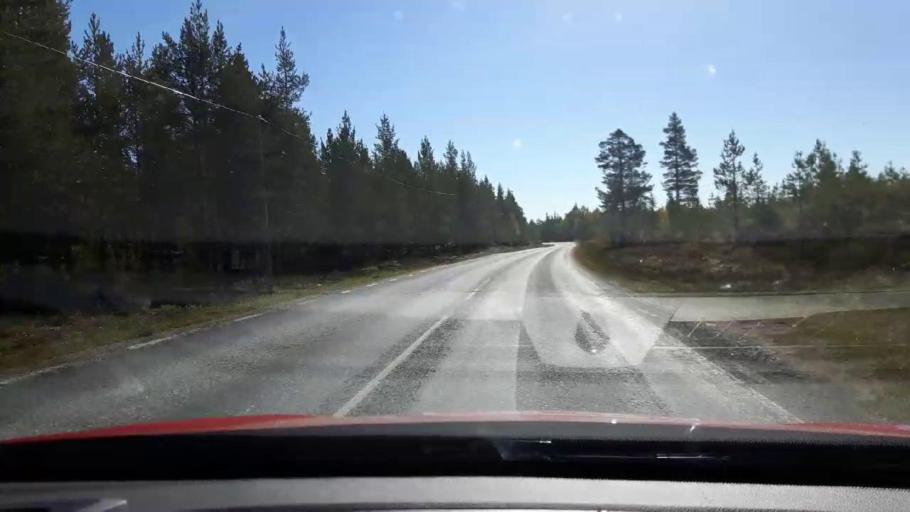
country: SE
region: Jaemtland
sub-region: Harjedalens Kommun
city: Sveg
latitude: 62.4296
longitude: 13.8911
